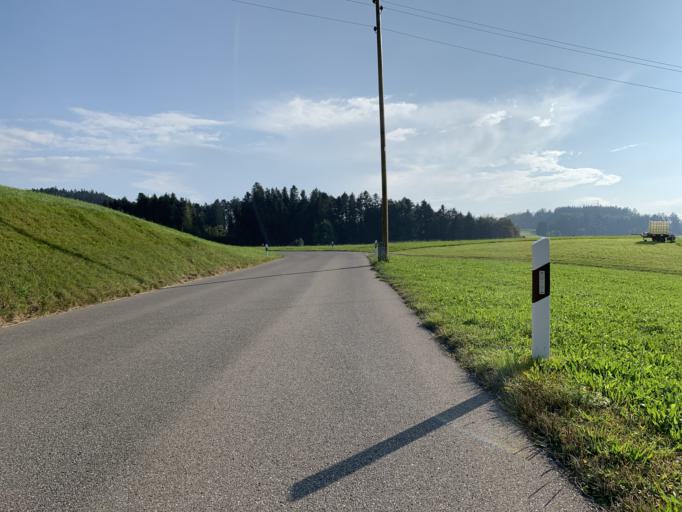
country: CH
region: Zurich
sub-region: Bezirk Hinwil
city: Baretswil
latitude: 47.3305
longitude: 8.8638
